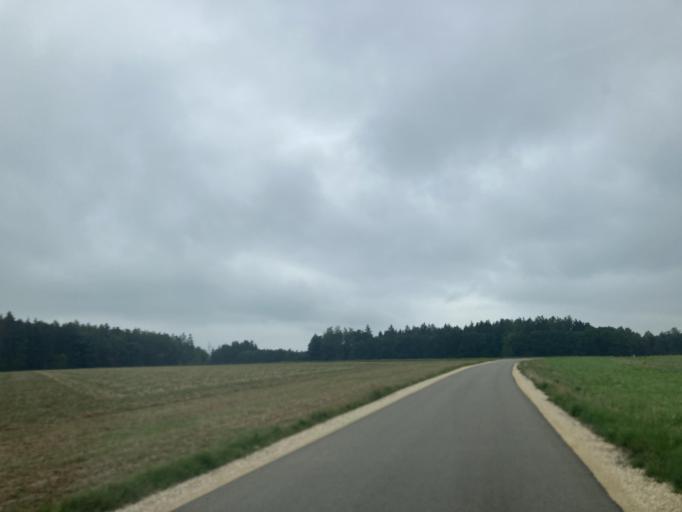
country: DE
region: Bavaria
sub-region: Swabia
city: Medlingen
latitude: 48.5795
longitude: 10.3095
